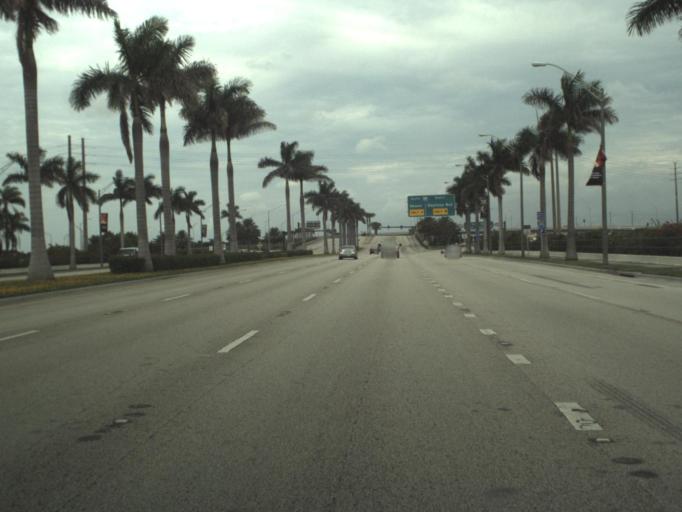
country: US
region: Florida
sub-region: Palm Beach County
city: West Palm Beach
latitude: 26.7059
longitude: -80.0702
